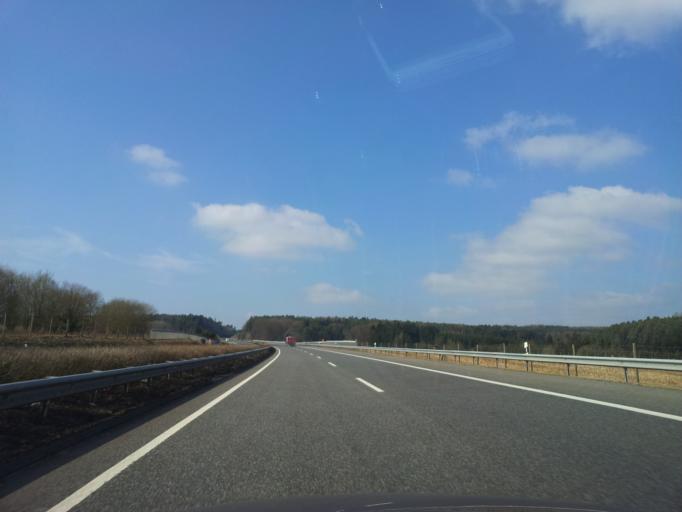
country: DE
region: Rheinland-Pfalz
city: Landscheid
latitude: 49.9980
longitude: 6.7607
